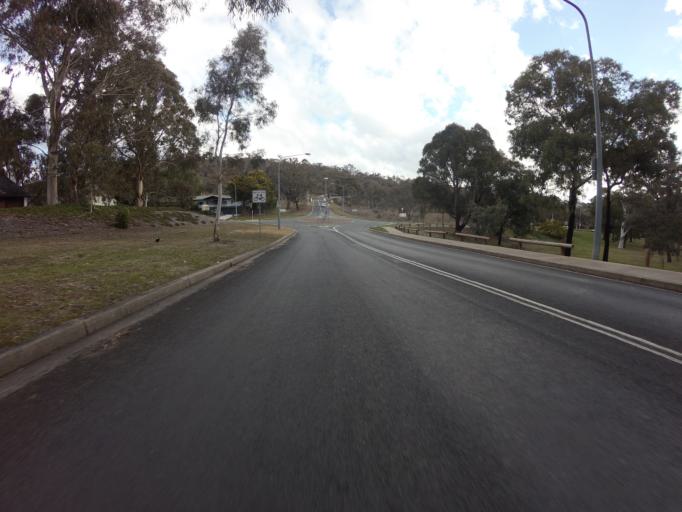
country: AU
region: Australian Capital Territory
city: Forrest
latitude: -35.3191
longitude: 149.1147
